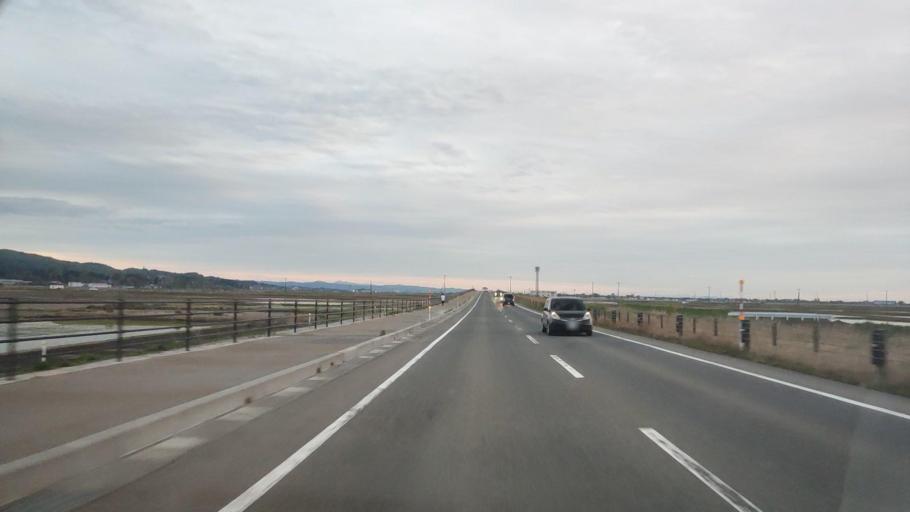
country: JP
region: Niigata
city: Shirone
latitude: 37.7451
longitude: 139.0833
